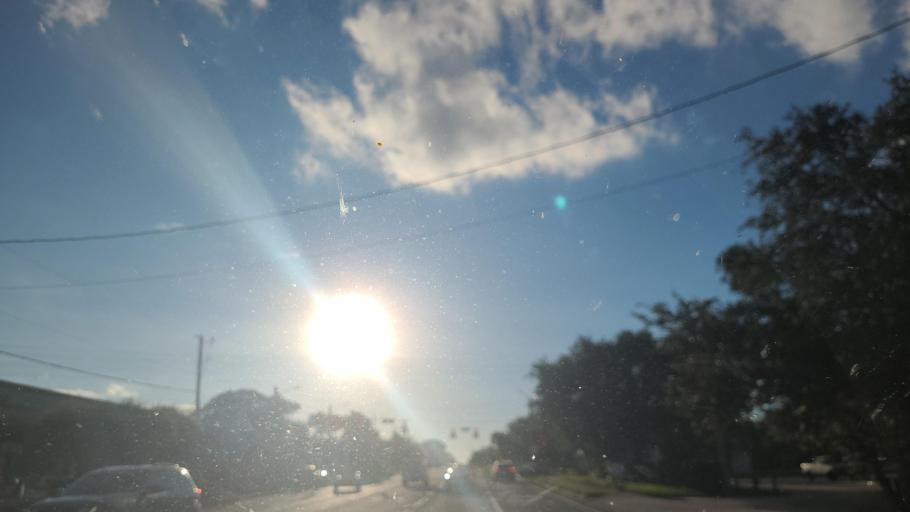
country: US
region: Florida
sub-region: Indian River County
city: Vero Beach South
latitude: 27.6088
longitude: -80.3878
